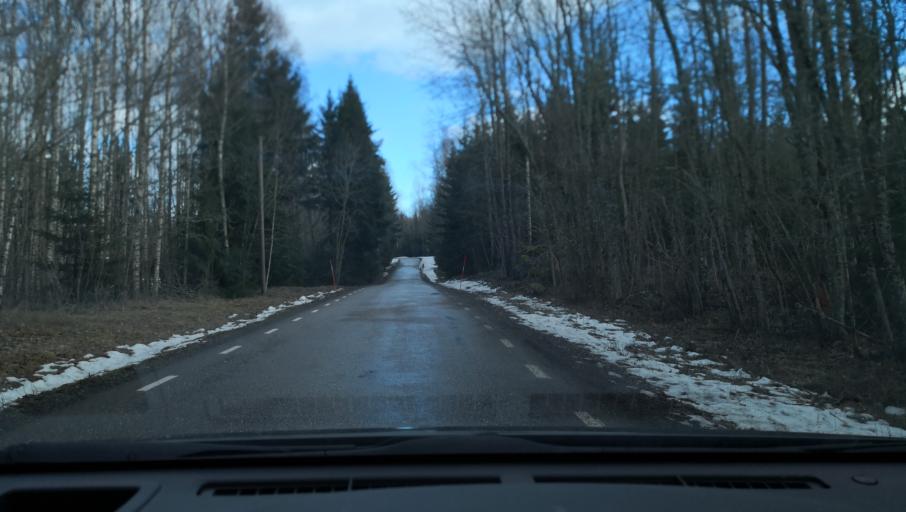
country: SE
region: Vaestmanland
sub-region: Arboga Kommun
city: Arboga
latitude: 59.3371
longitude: 15.7065
